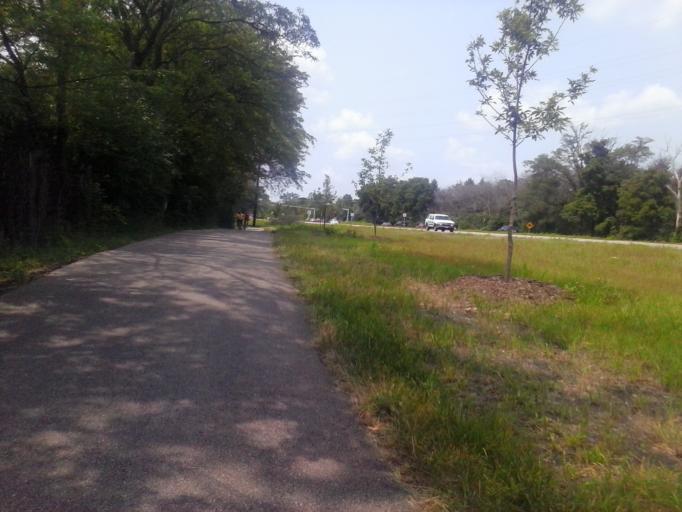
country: US
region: Illinois
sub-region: DuPage County
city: Warrenville
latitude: 41.8300
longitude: -88.1647
